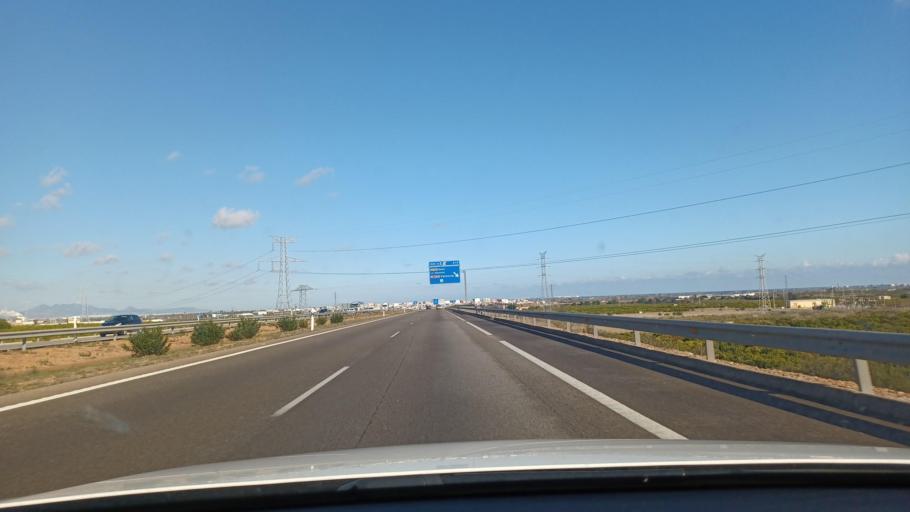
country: ES
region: Valencia
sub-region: Provincia de Castello
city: Villavieja
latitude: 39.8388
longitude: -0.1894
